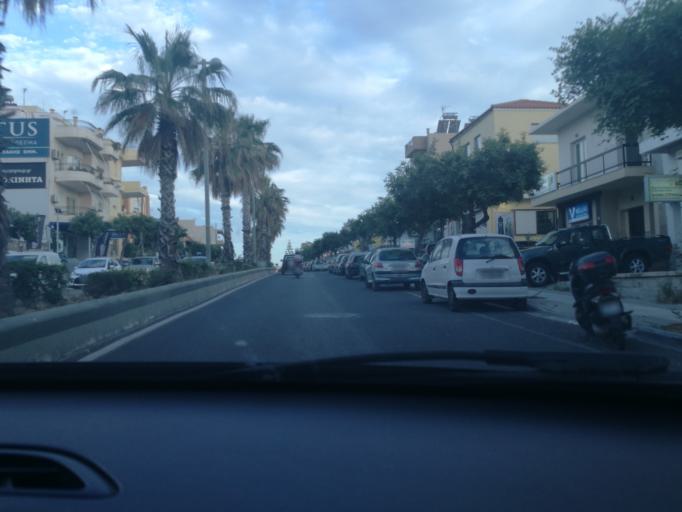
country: GR
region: Crete
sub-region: Nomos Irakleiou
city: Irakleion
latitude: 35.3174
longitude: 25.1454
